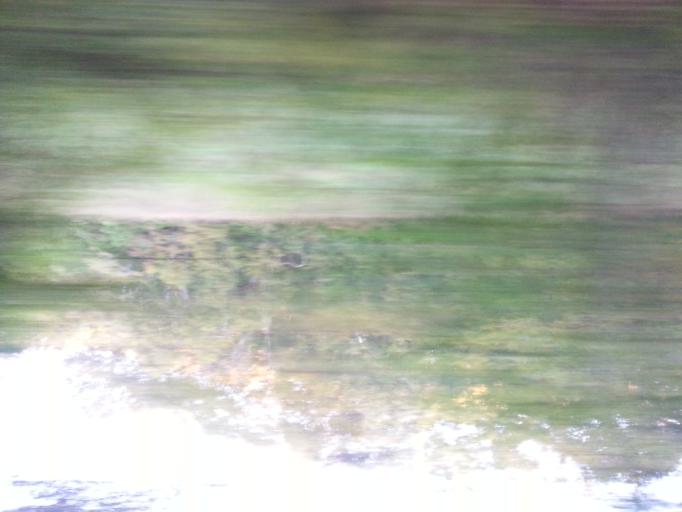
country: US
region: Tennessee
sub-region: Sevier County
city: Seymour
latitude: 35.7866
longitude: -83.7398
